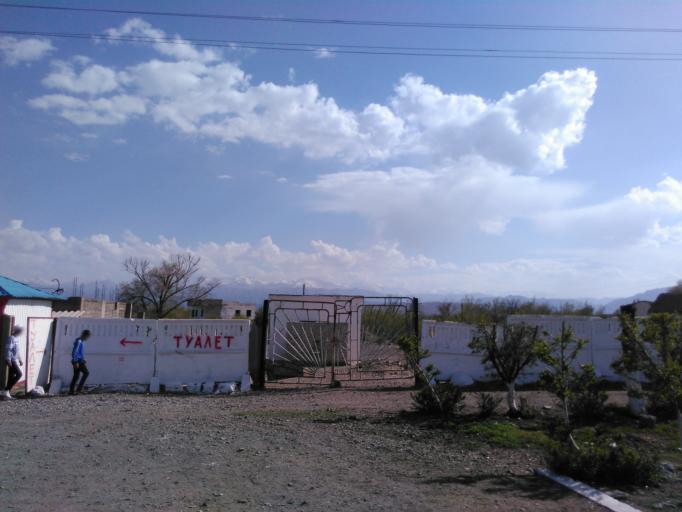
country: KG
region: Ysyk-Koel
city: Balykchy
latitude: 42.4525
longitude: 76.1658
